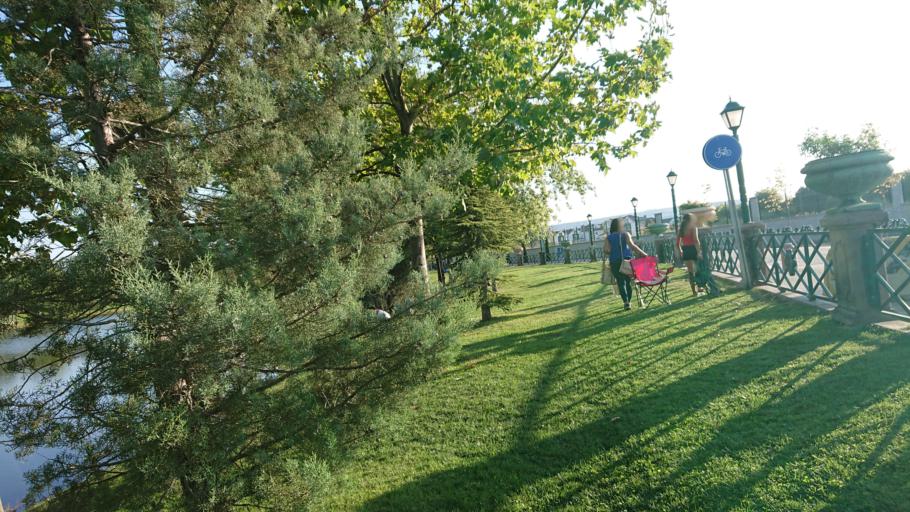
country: TR
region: Eskisehir
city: Eskisehir
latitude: 39.7646
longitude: 30.4860
